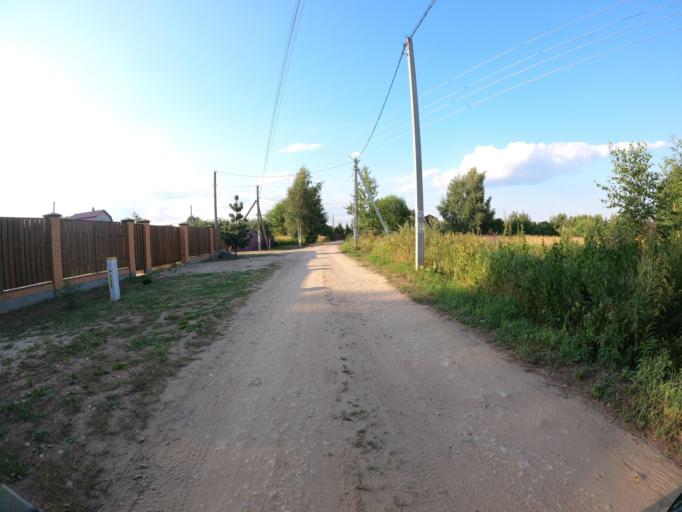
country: RU
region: Moskovskaya
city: Bronnitsy
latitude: 55.4827
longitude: 38.2586
